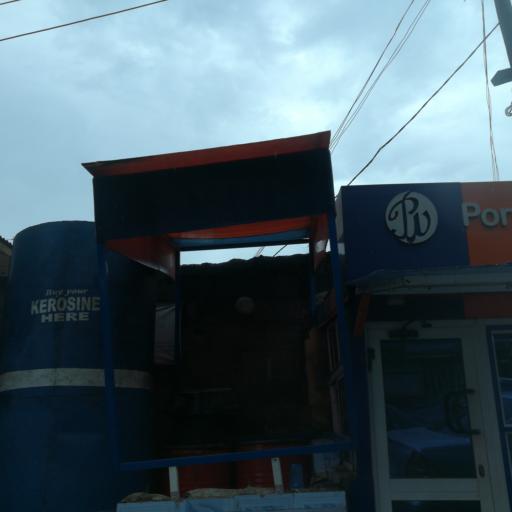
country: NG
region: Lagos
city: Oshodi
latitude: 6.5553
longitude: 3.3465
